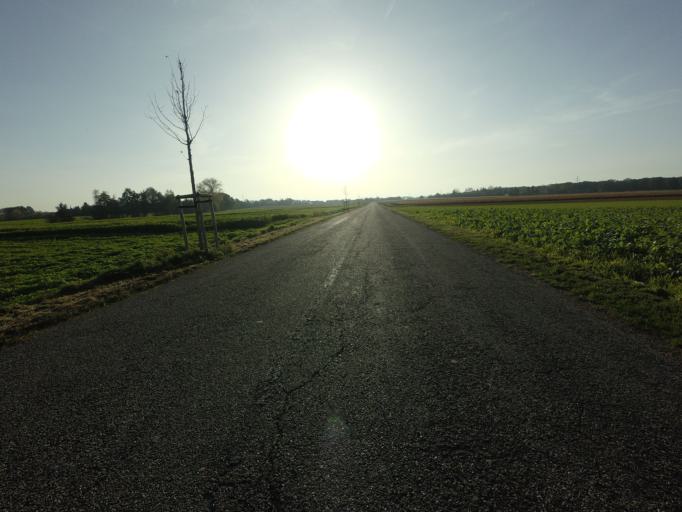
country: DE
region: North Rhine-Westphalia
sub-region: Regierungsbezirk Koln
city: Waldfeucht
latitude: 51.0821
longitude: 5.9995
